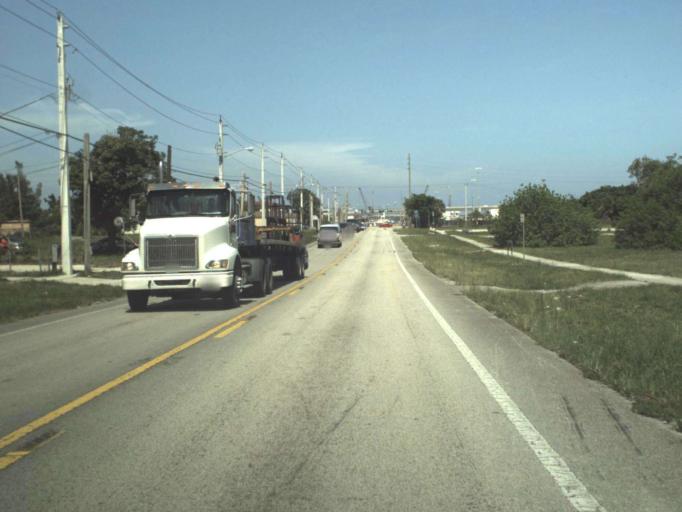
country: US
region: Florida
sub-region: Palm Beach County
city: Riviera Beach
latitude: 26.7693
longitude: -80.0650
